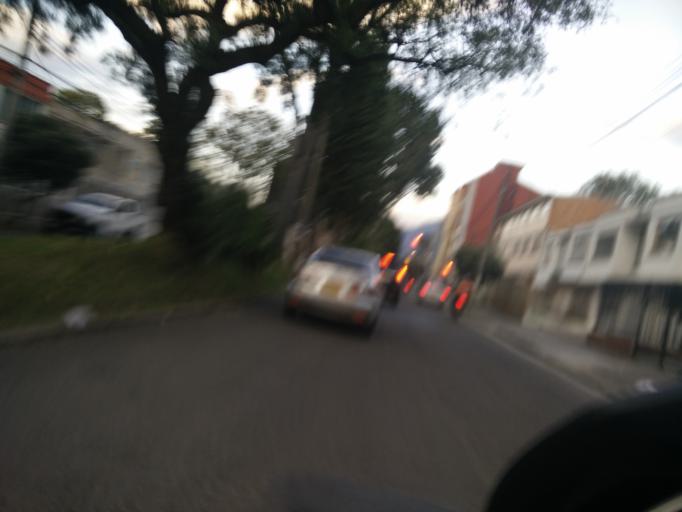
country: CO
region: Bogota D.C.
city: Bogota
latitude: 4.6480
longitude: -74.0725
